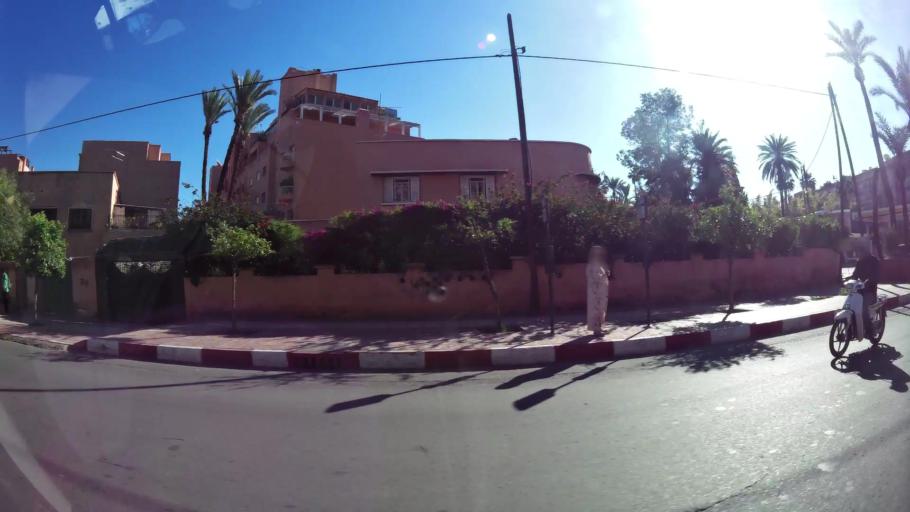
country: MA
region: Marrakech-Tensift-Al Haouz
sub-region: Marrakech
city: Marrakesh
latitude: 31.6399
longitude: -8.0050
